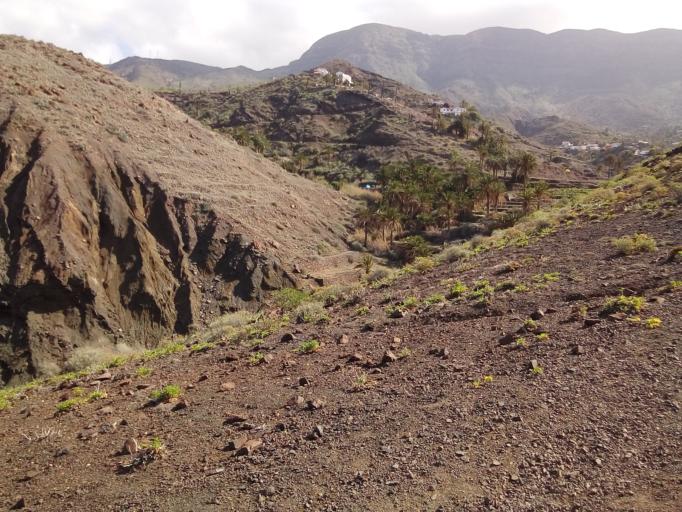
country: ES
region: Canary Islands
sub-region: Provincia de Santa Cruz de Tenerife
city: Vallehermosa
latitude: 28.1706
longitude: -17.3349
